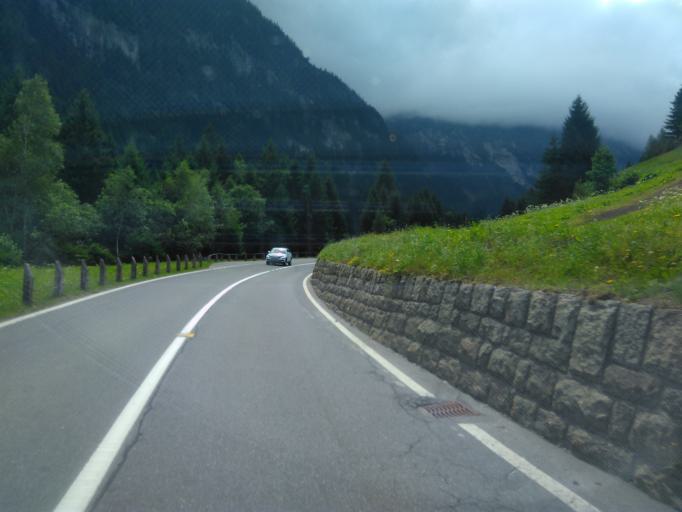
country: CH
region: Uri
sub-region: Uri
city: Andermatt
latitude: 46.6822
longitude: 8.5934
